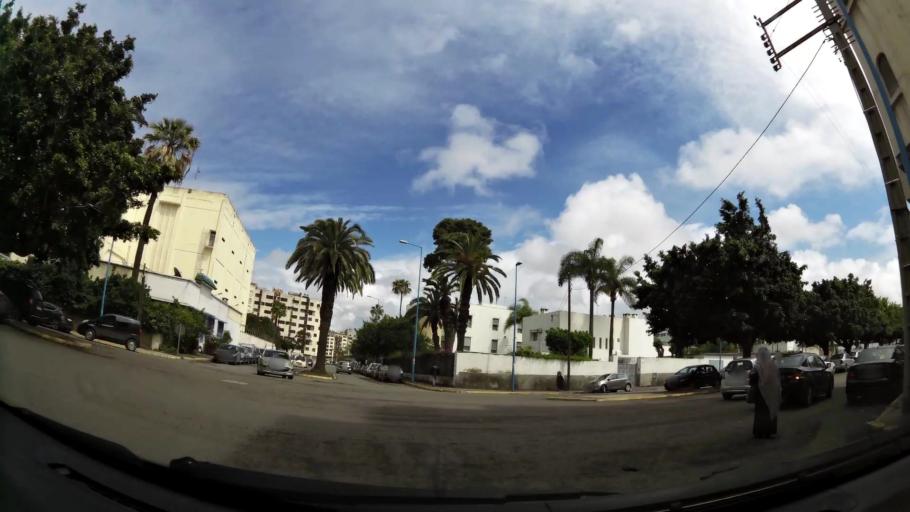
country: MA
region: Grand Casablanca
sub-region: Casablanca
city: Casablanca
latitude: 33.5819
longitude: -7.6220
